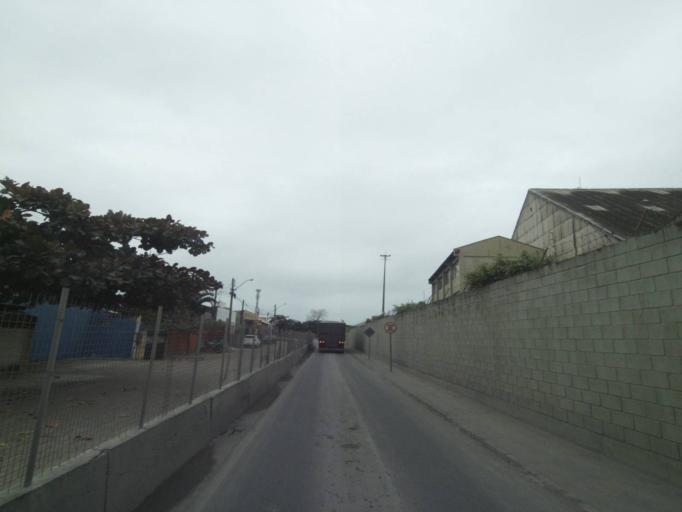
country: BR
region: Parana
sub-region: Paranagua
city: Paranagua
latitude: -25.5365
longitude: -48.5364
